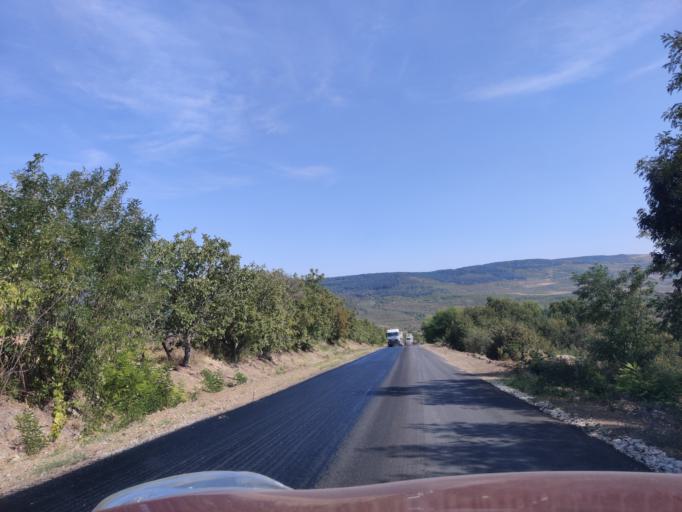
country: MD
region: Ungheni
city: Ungheni
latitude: 47.2594
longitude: 27.9848
